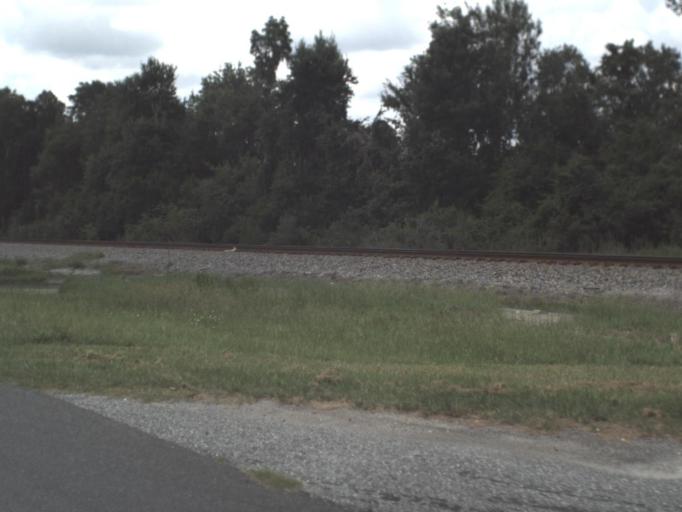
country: US
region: Florida
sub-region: Hamilton County
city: Jasper
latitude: 30.4177
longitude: -82.8530
